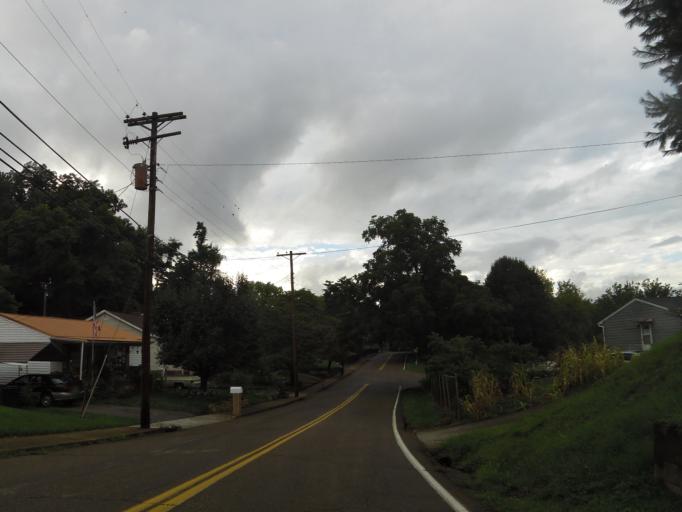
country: US
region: Tennessee
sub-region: Knox County
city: Knoxville
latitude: 35.9531
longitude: -83.9050
